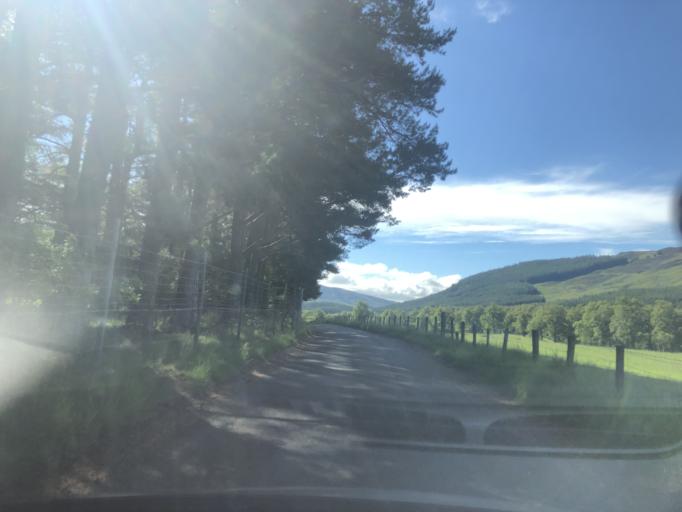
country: GB
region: Scotland
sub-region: Angus
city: Kirriemuir
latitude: 56.8364
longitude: -3.0829
